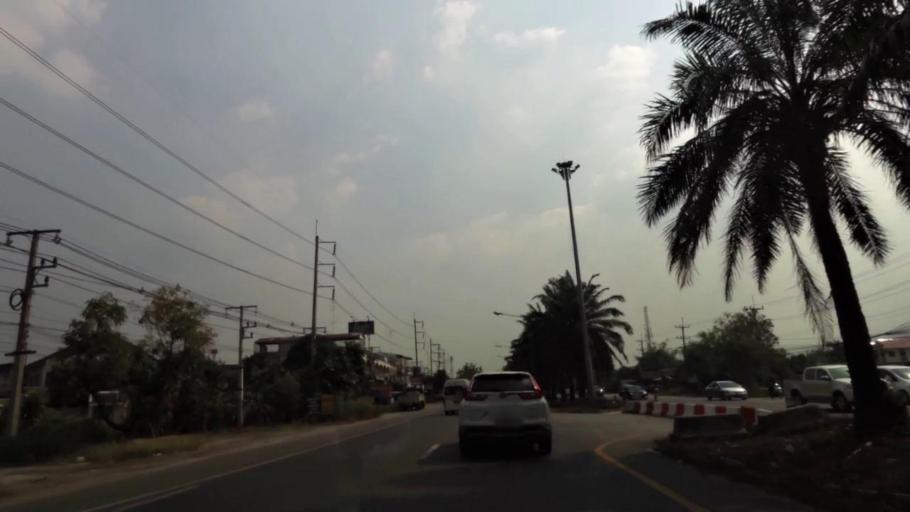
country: TH
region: Chon Buri
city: Ban Bueng
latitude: 13.3065
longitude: 101.1093
